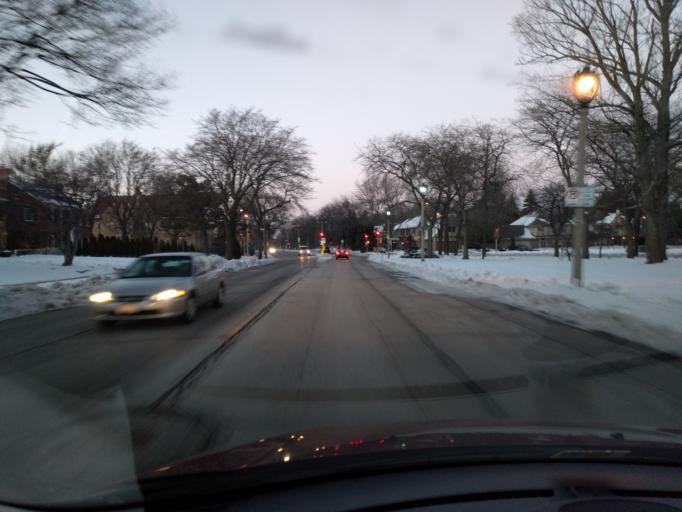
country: US
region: Wisconsin
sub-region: Milwaukee County
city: Shorewood
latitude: 43.0738
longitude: -87.8721
